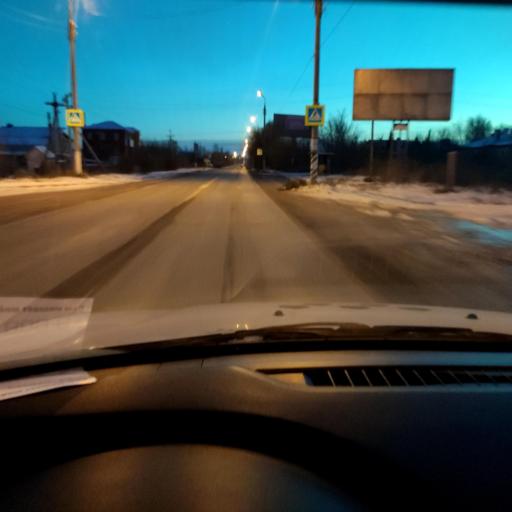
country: RU
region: Samara
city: Tol'yatti
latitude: 53.5629
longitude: 49.3958
